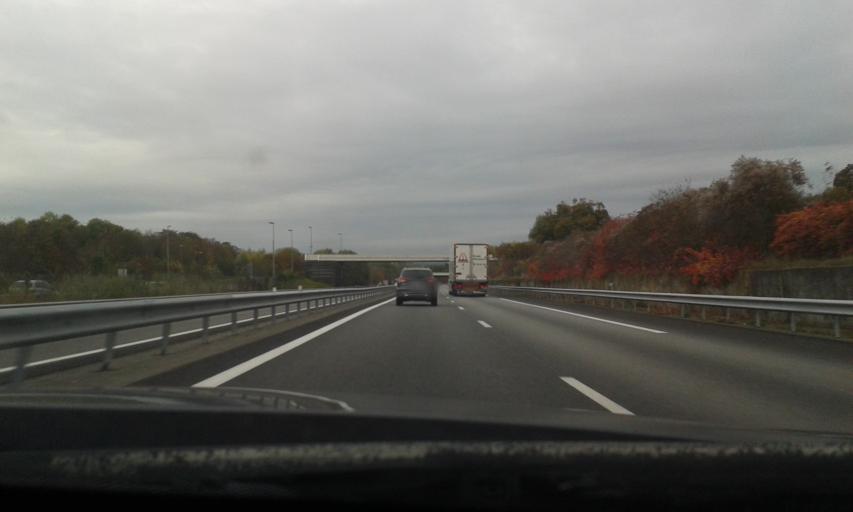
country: FR
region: Haute-Normandie
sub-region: Departement de l'Eure
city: Louviers
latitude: 49.2181
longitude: 1.1801
